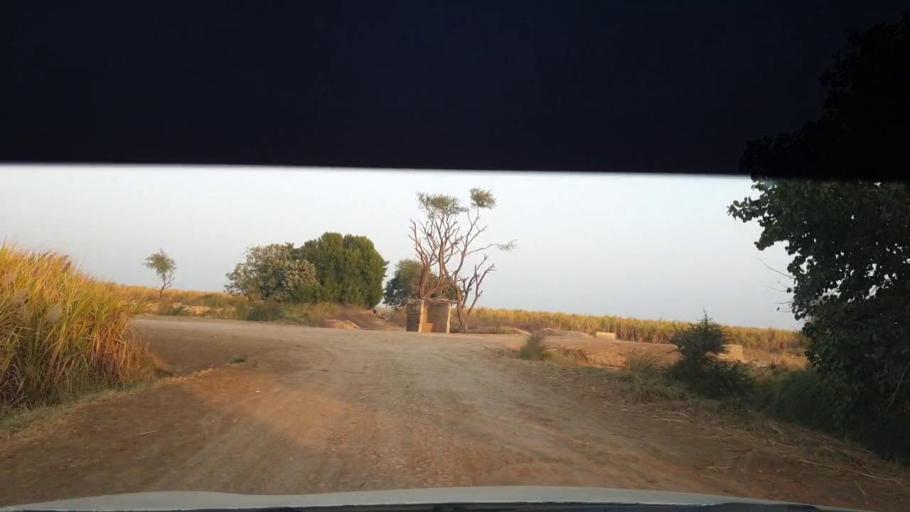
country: PK
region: Sindh
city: Berani
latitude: 25.7531
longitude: 69.0070
